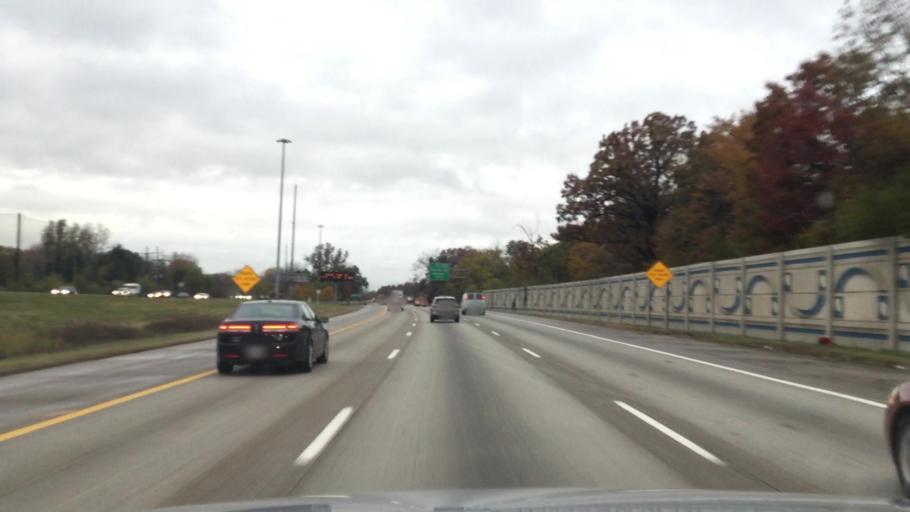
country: US
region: Michigan
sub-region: Wayne County
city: Taylor
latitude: 42.2630
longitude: -83.2865
